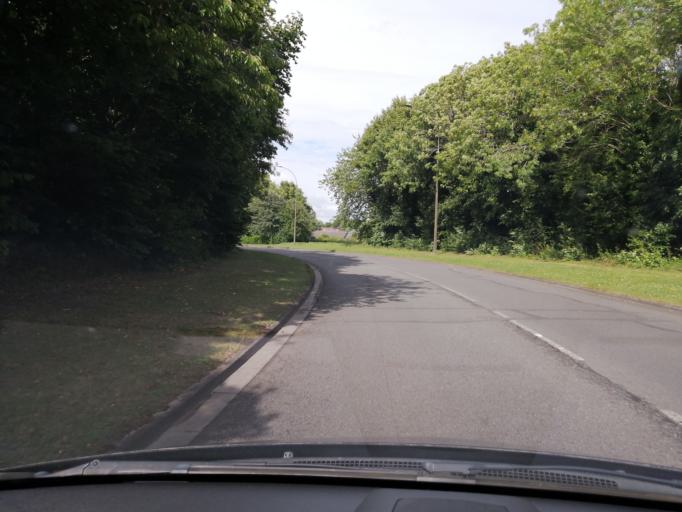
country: GB
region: England
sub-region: Peterborough
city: Castor
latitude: 52.5501
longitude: -0.3021
